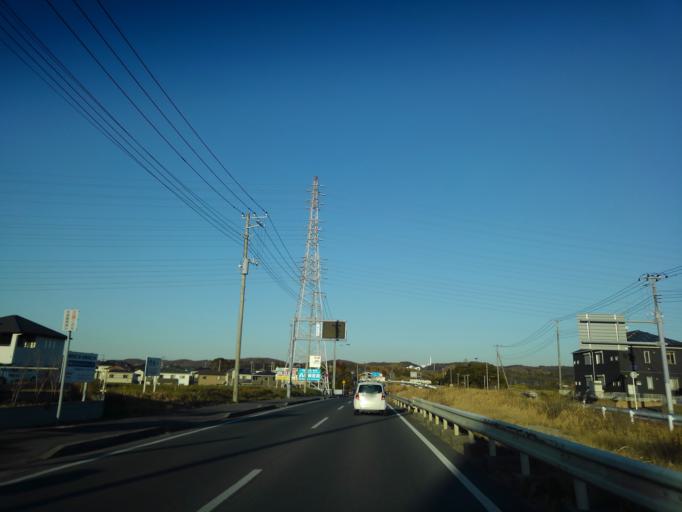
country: JP
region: Chiba
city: Kimitsu
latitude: 35.3099
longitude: 139.9232
